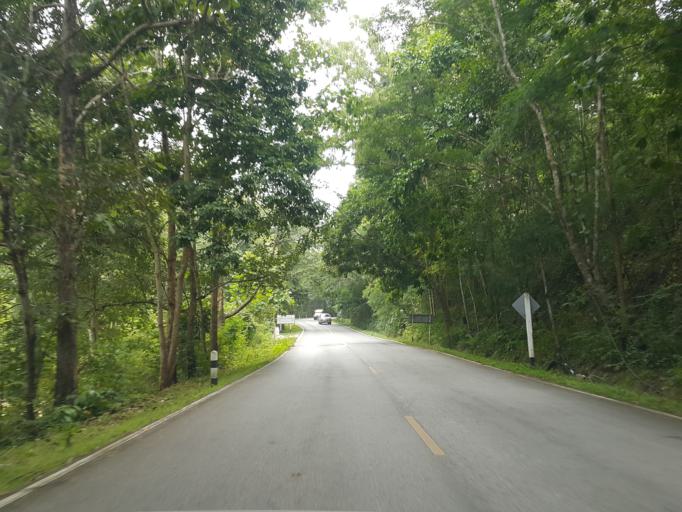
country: TH
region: Mae Hong Son
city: Mae Hi
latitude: 19.2788
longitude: 98.4945
